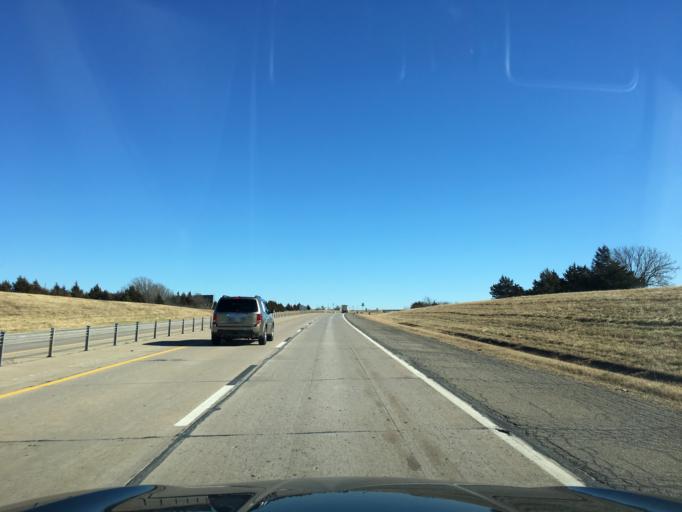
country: US
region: Oklahoma
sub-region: Pawnee County
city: Pawnee
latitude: 36.2394
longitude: -96.9361
